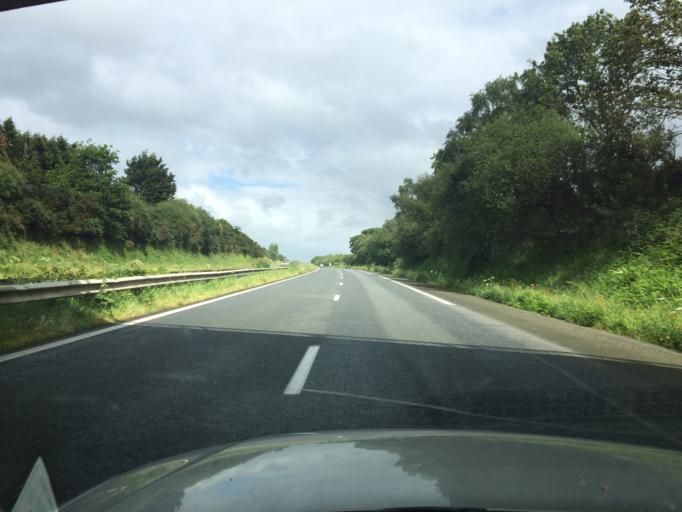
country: FR
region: Brittany
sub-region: Departement du Finistere
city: Bodilis
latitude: 48.5027
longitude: -4.1546
